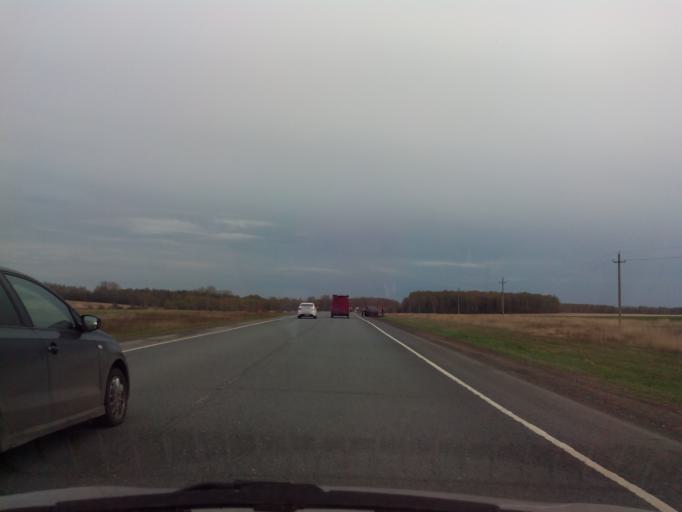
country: RU
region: Moskovskaya
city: Ozherel'ye
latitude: 54.6391
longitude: 38.3734
